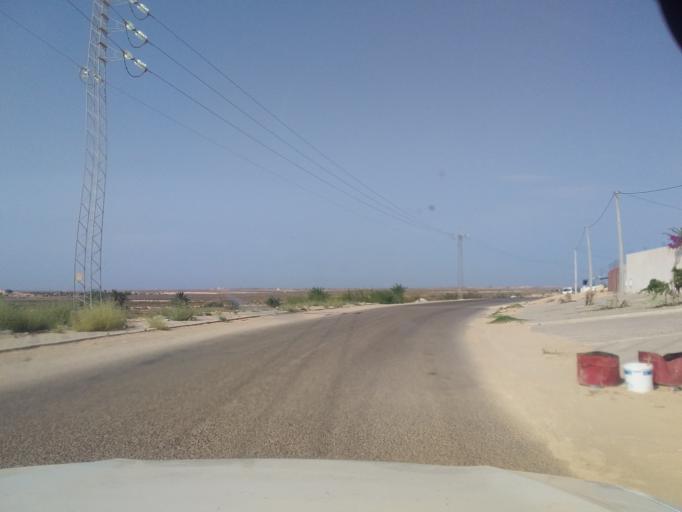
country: TN
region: Qabis
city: Gabes
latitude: 33.6371
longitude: 10.2841
